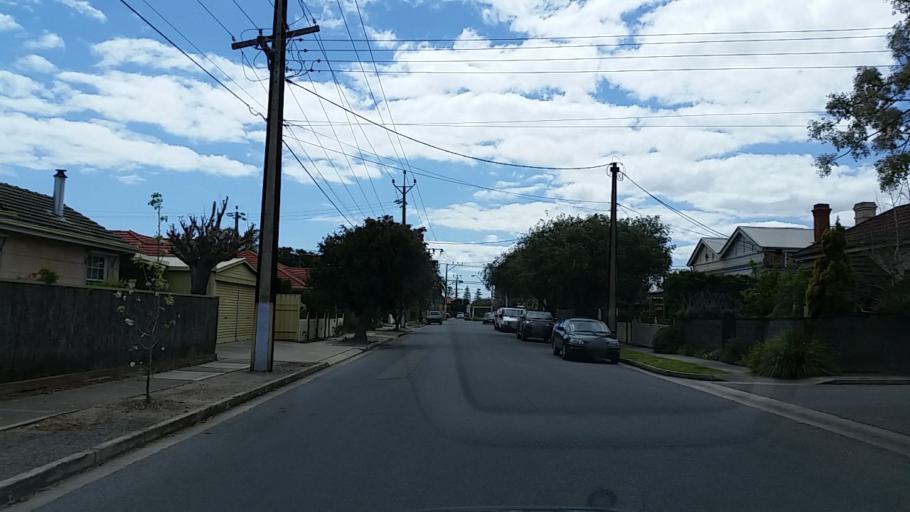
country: AU
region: South Australia
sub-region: Adelaide
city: Glenelg
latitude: -34.9925
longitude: 138.5160
